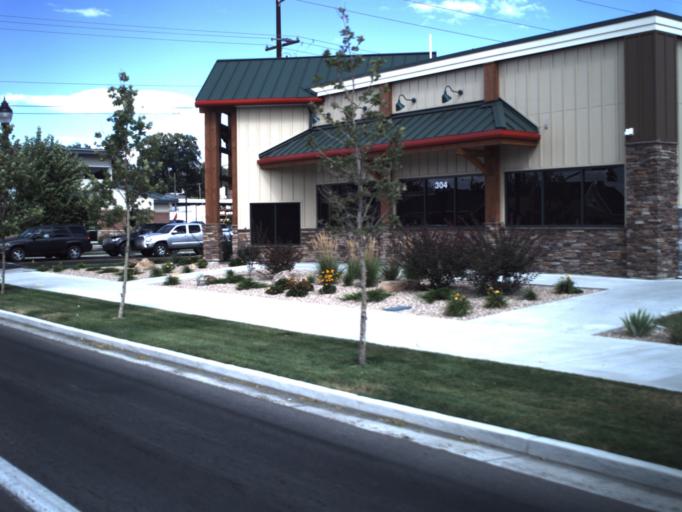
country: US
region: Utah
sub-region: Cache County
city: Logan
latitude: 41.7255
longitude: -111.8351
